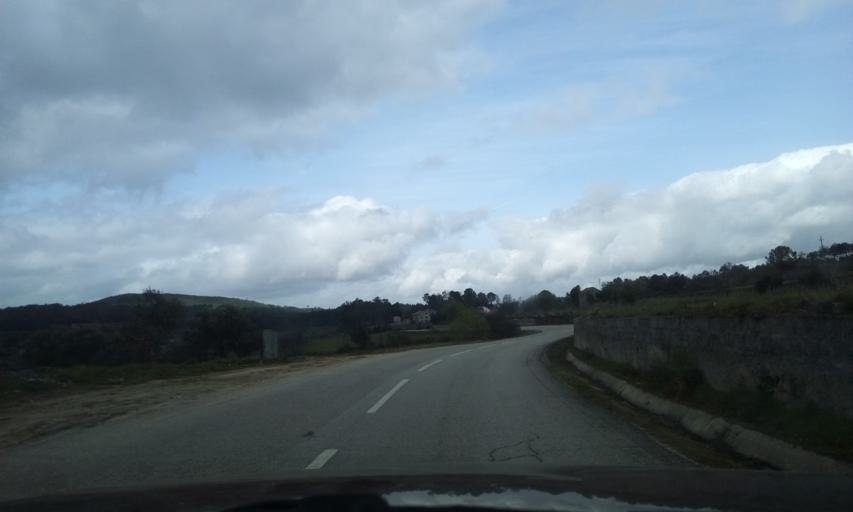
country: PT
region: Guarda
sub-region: Fornos de Algodres
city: Fornos de Algodres
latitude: 40.6596
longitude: -7.5938
